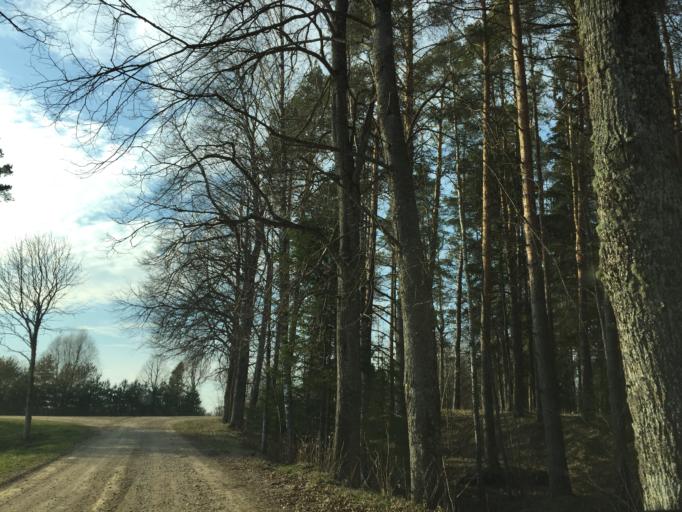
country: EE
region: Jogevamaa
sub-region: Mustvee linn
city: Mustvee
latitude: 58.8611
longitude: 26.8390
